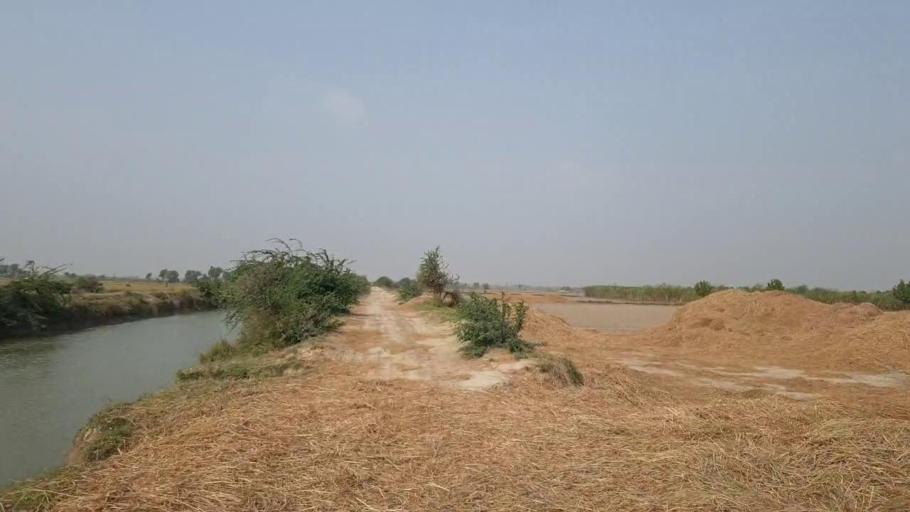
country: PK
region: Sindh
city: Kario
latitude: 24.8497
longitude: 68.5314
